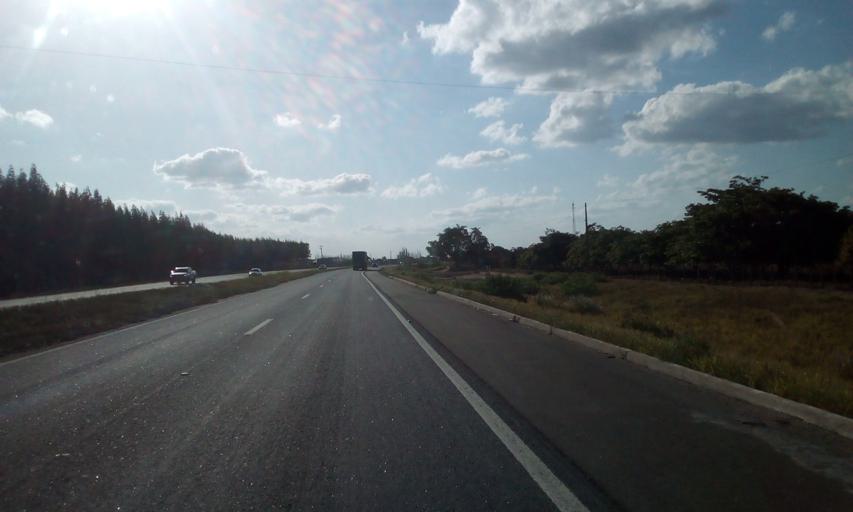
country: BR
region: Paraiba
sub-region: Cruz Do Espirito Santo
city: Cruz do Espirito Santo
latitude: -7.2054
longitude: -35.1451
